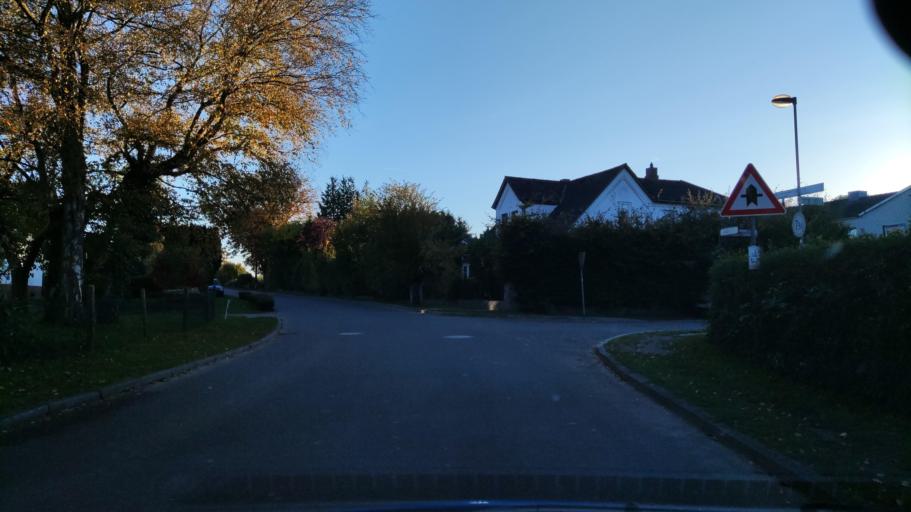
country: DE
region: Schleswig-Holstein
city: Basthorst
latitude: 53.5751
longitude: 10.4723
